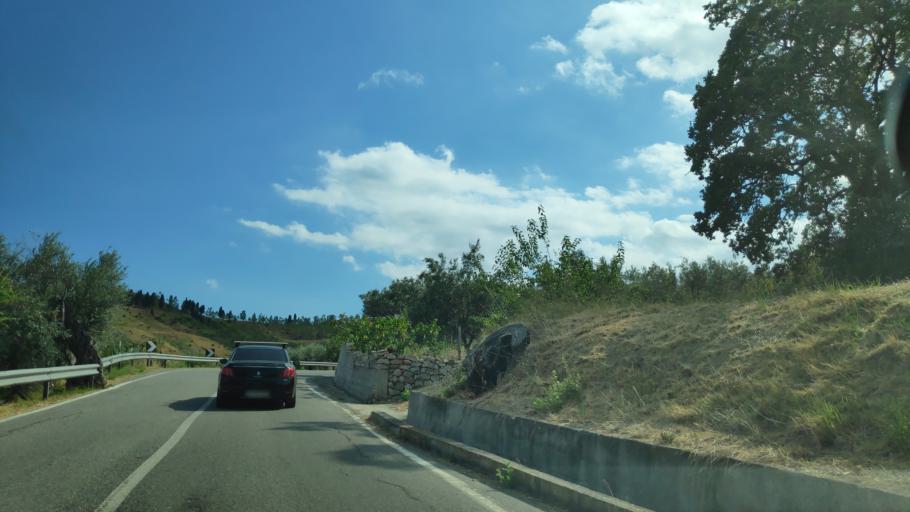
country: IT
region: Calabria
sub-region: Provincia di Catanzaro
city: Santa Caterina dello Ionio Marina
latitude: 38.5283
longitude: 16.5507
